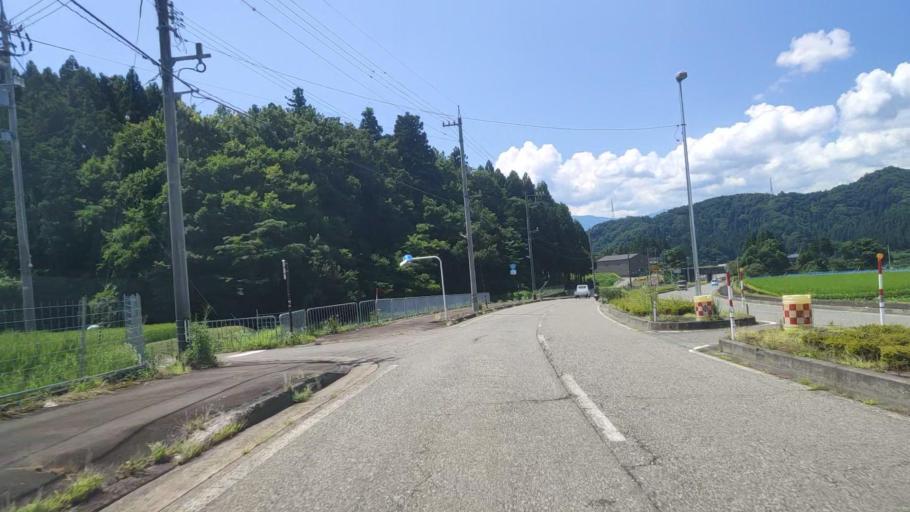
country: JP
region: Fukui
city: Katsuyama
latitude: 36.0313
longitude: 136.5203
